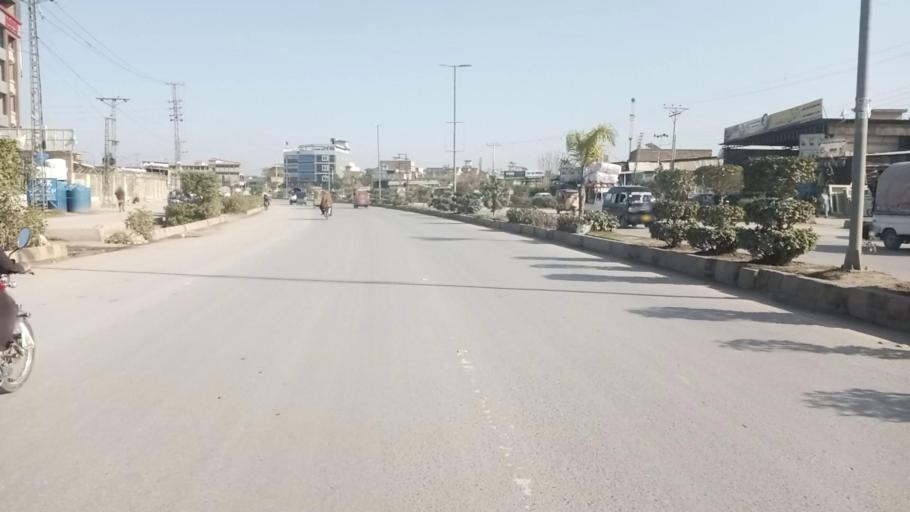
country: PK
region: Khyber Pakhtunkhwa
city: Peshawar
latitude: 34.0308
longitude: 71.5929
